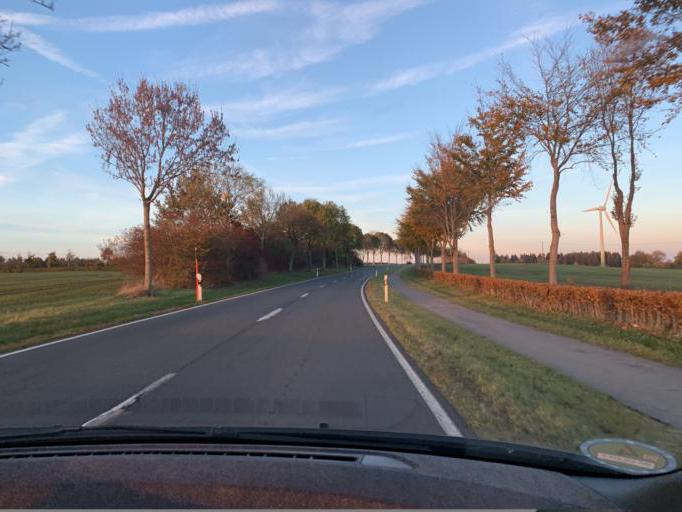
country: DE
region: North Rhine-Westphalia
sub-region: Regierungsbezirk Koln
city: Simmerath
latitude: 50.6400
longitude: 6.3452
